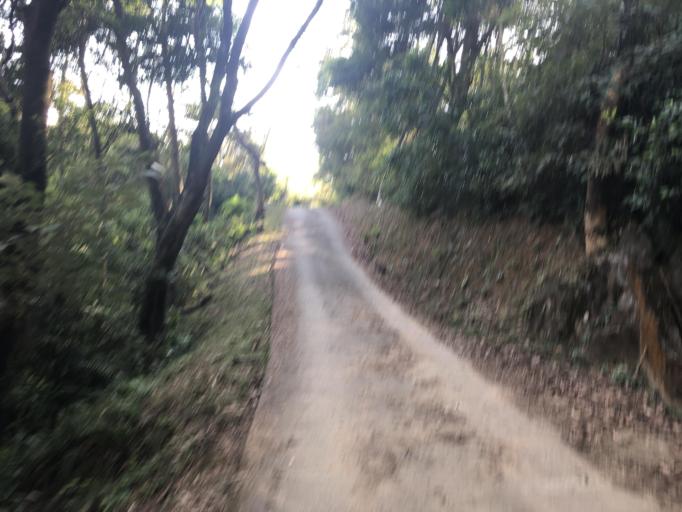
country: HK
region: Tsuen Wan
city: Tsuen Wan
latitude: 22.3908
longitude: 114.0853
